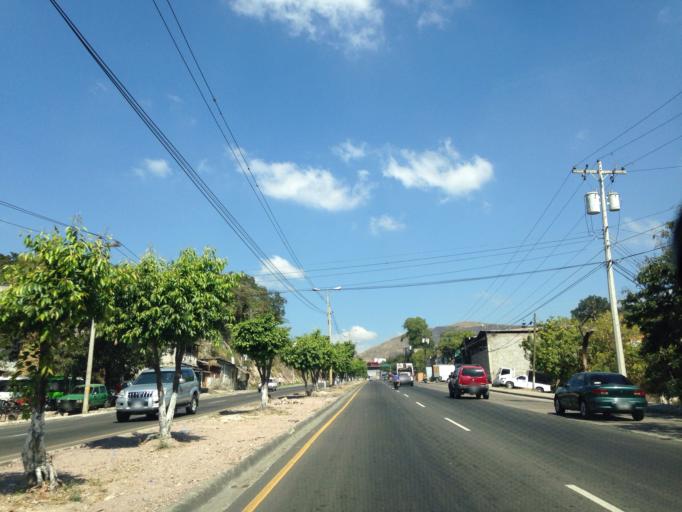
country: HN
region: Francisco Morazan
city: El Lolo
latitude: 14.0991
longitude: -87.2407
